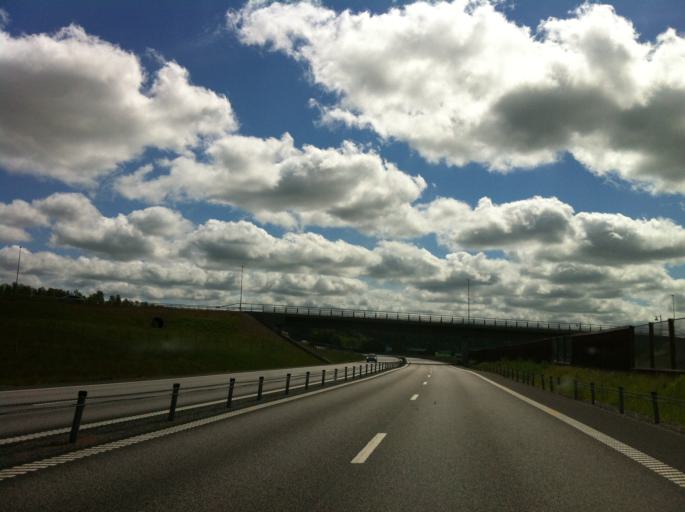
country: SE
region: Vaestra Goetaland
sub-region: Lilla Edets Kommun
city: Lodose
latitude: 58.0051
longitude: 12.1604
